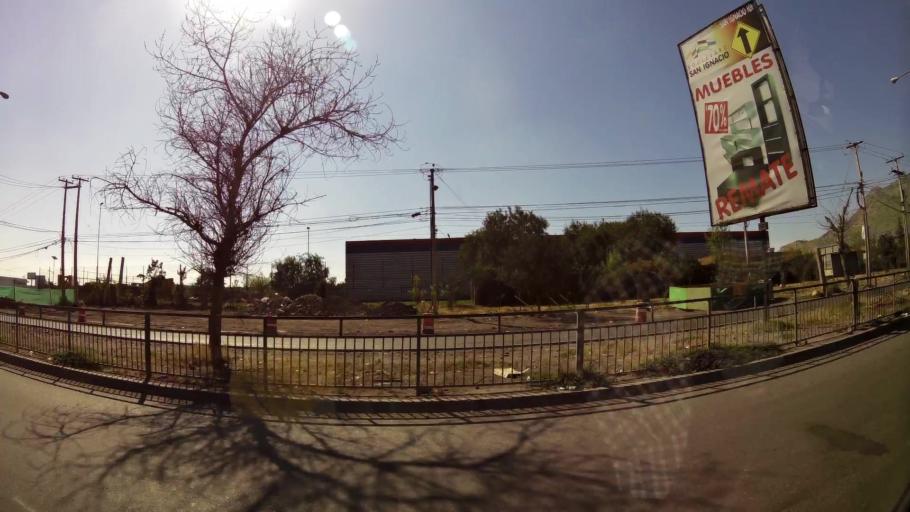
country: CL
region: Santiago Metropolitan
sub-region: Provincia de Chacabuco
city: Chicureo Abajo
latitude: -33.3334
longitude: -70.7122
